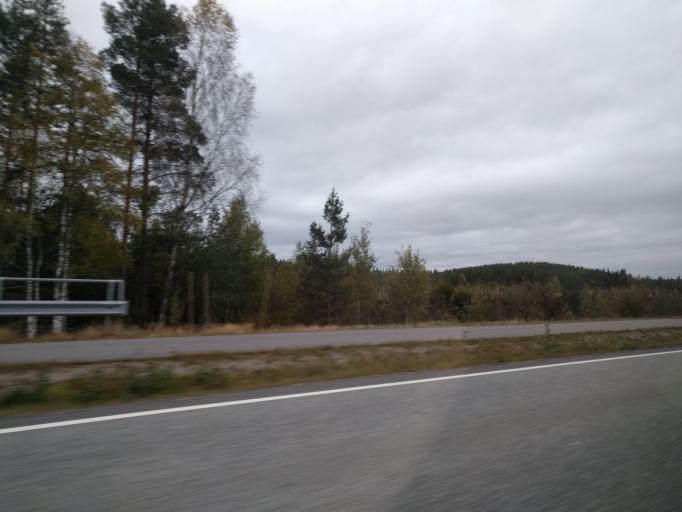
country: NO
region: Aust-Agder
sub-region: Evje og Hornnes
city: Evje
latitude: 58.5814
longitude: 7.7943
